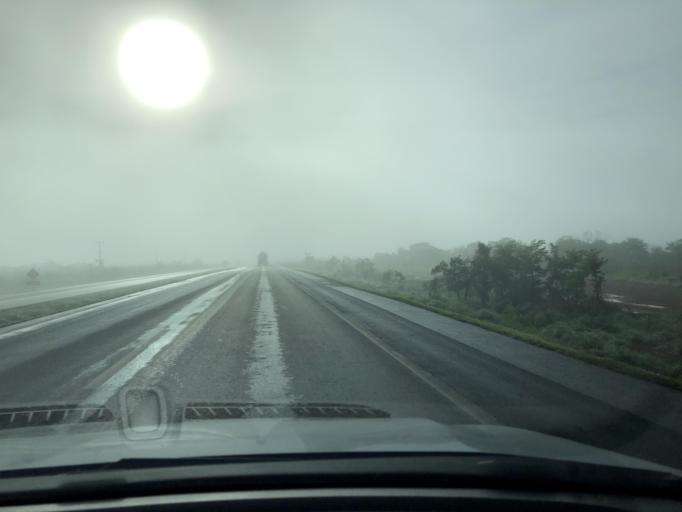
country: BR
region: Goias
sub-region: Luziania
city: Luziania
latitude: -16.2701
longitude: -47.8799
